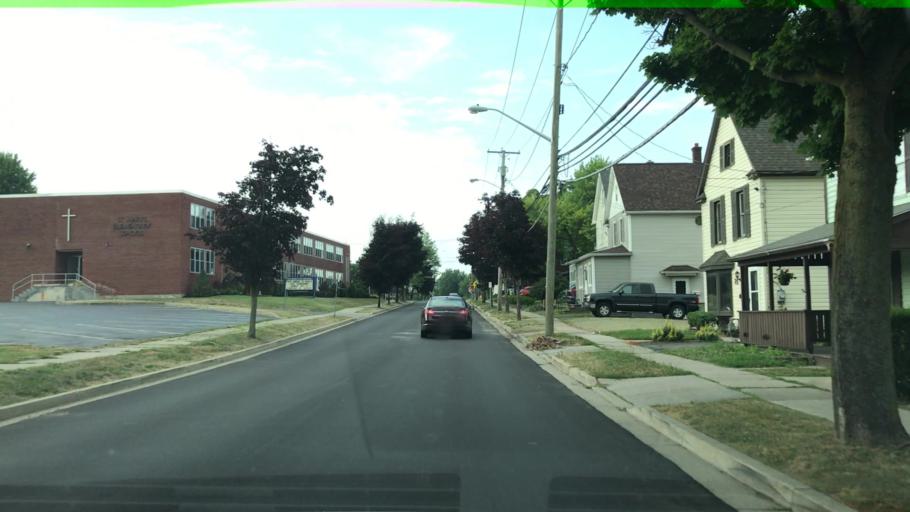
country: US
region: New York
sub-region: Erie County
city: Lancaster
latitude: 42.9028
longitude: -78.6731
